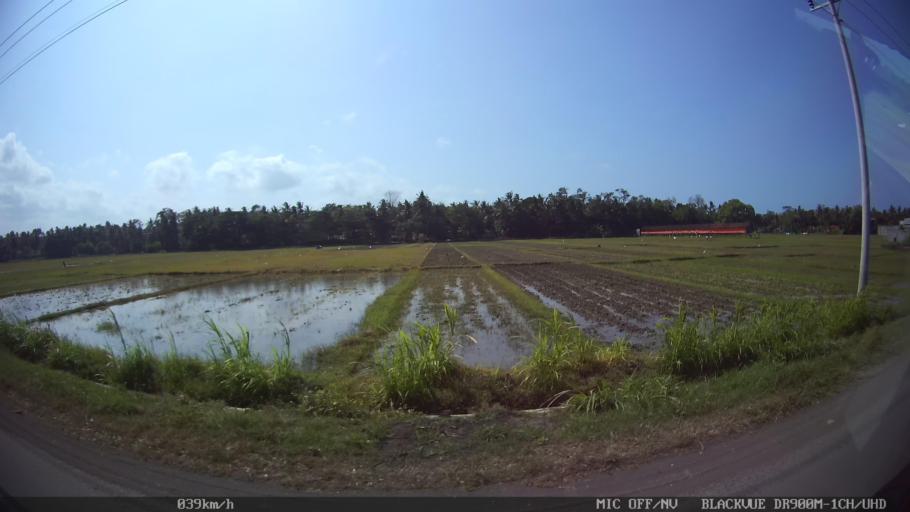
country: ID
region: Daerah Istimewa Yogyakarta
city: Srandakan
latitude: -7.9568
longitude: 110.2167
